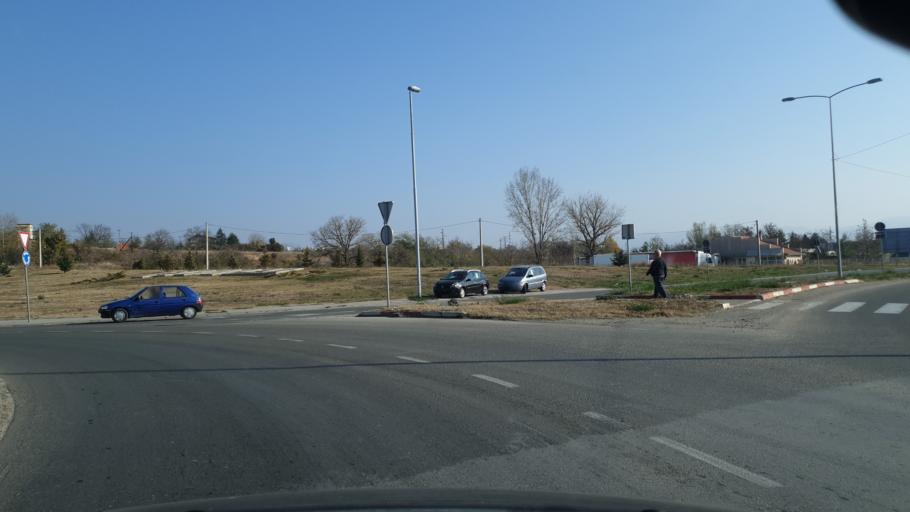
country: RS
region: Central Serbia
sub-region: Nisavski Okrug
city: Nis
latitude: 43.3177
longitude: 21.8290
